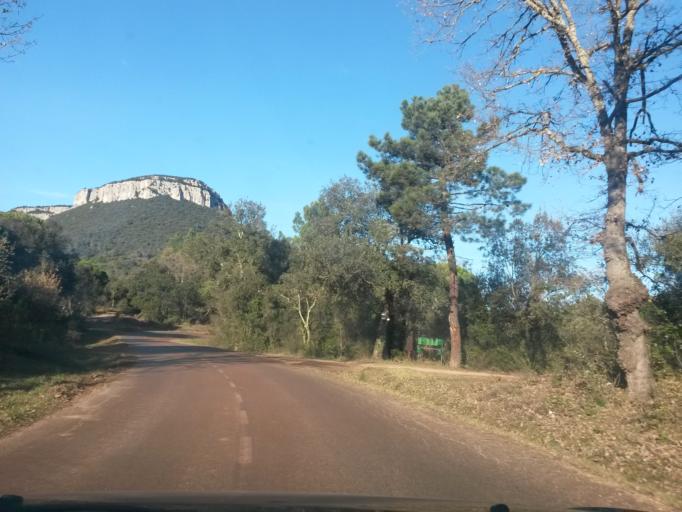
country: ES
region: Catalonia
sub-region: Provincia de Girona
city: Sant Gregori
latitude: 42.0118
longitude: 2.6746
